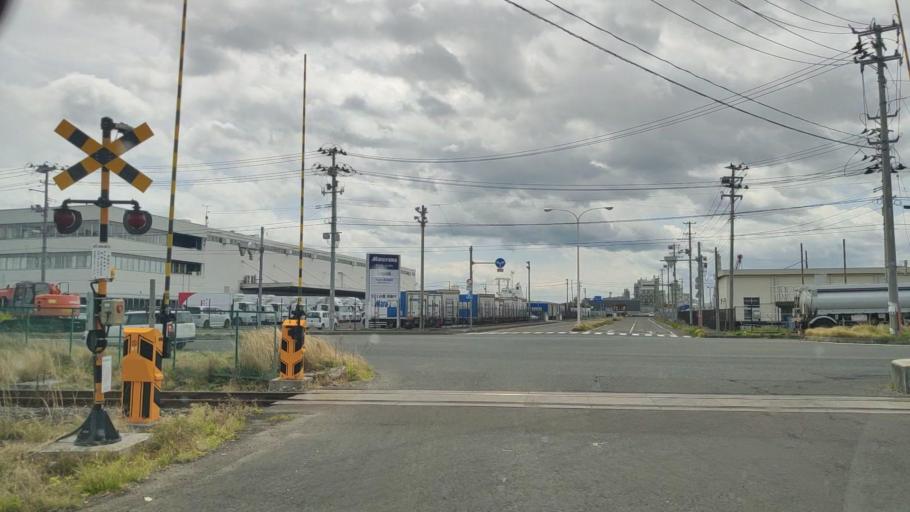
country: JP
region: Miyagi
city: Shiogama
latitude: 38.2768
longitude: 141.0102
